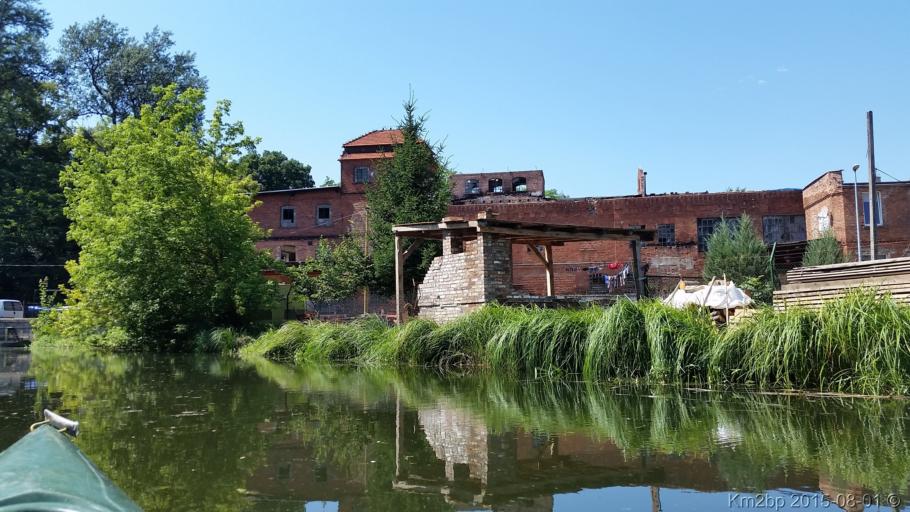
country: PL
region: Lubusz
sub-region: Powiat slubicki
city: Cybinka
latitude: 52.2375
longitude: 14.7846
